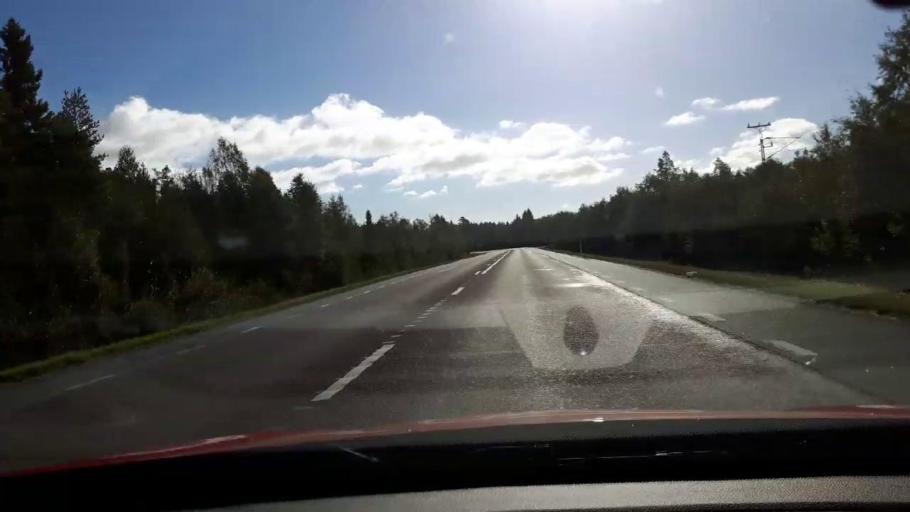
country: SE
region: Jaemtland
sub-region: Braecke Kommun
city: Braecke
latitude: 62.8167
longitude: 15.3425
